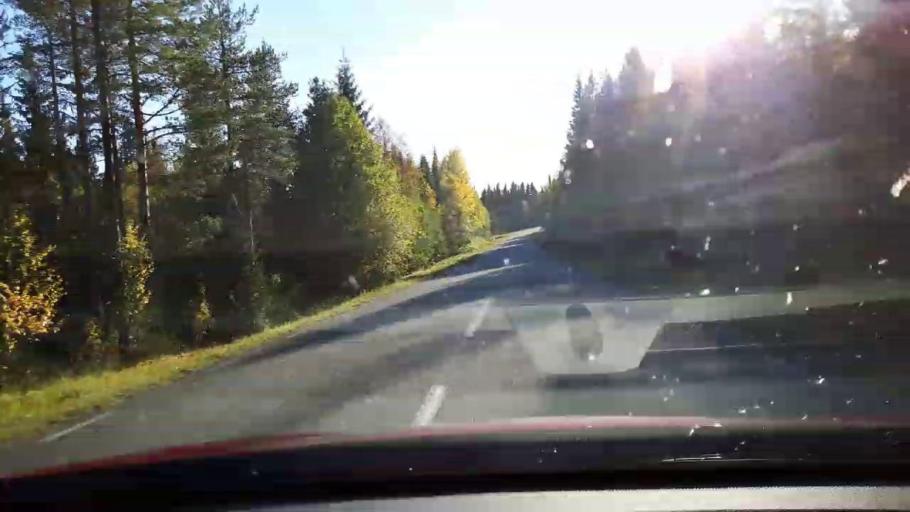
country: SE
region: Jaemtland
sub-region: OEstersunds Kommun
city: Lit
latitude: 63.8292
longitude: 14.8699
